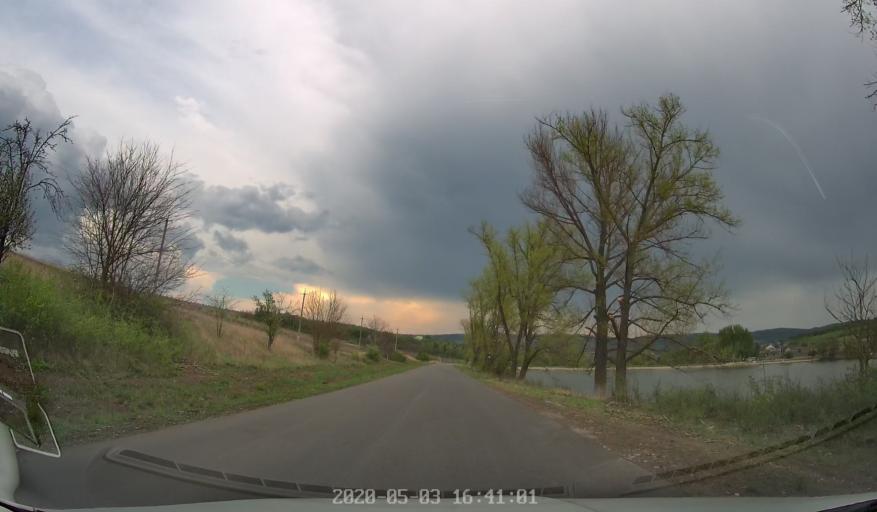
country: MD
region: Stinga Nistrului
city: Bucovat
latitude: 47.1702
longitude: 28.4014
